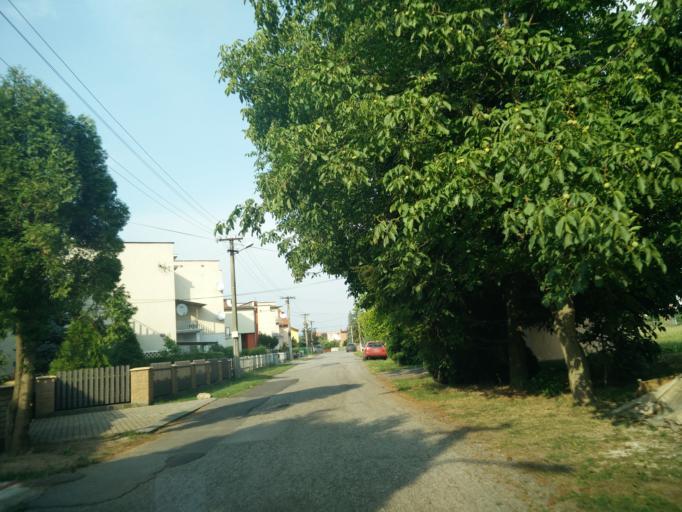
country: SK
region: Banskobystricky
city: Ziar nad Hronom
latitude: 48.5383
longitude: 18.7822
